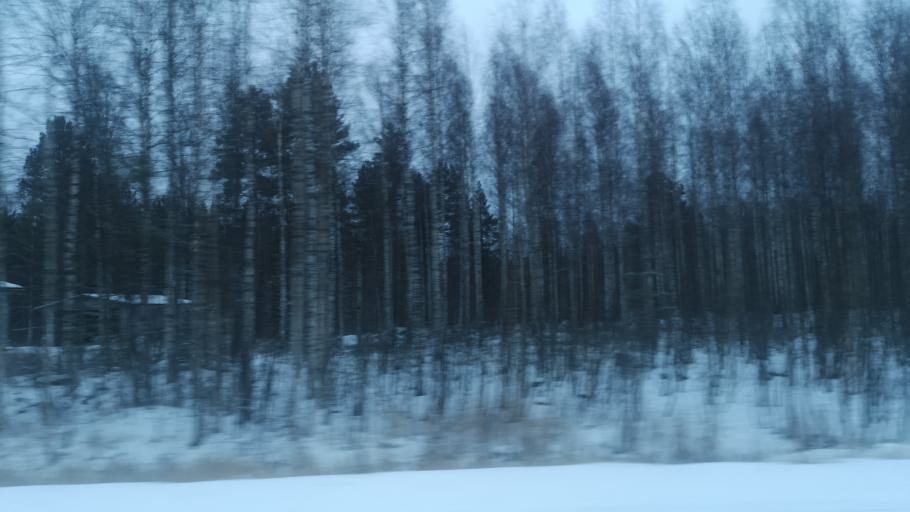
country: FI
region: Southern Savonia
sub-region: Savonlinna
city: Enonkoski
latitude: 62.1008
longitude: 28.6535
